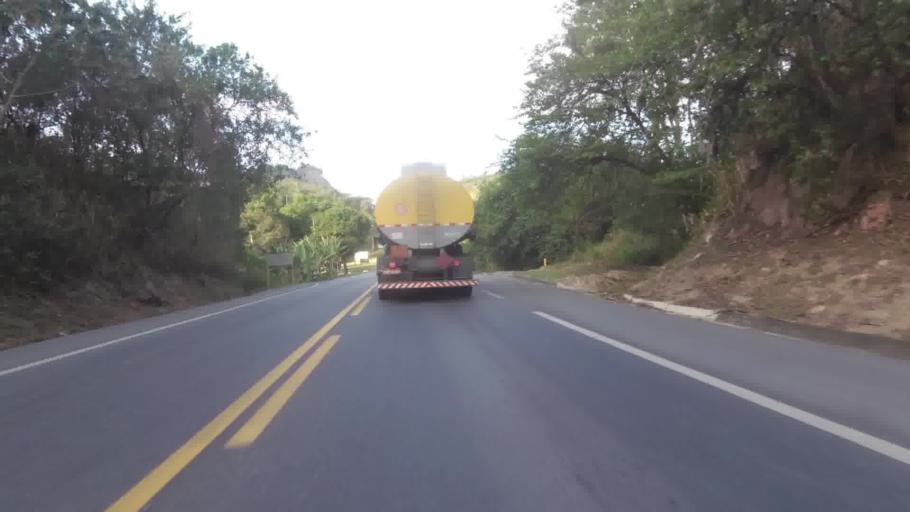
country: BR
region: Espirito Santo
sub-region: Rio Novo Do Sul
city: Rio Novo do Sul
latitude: -20.8925
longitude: -41.0012
